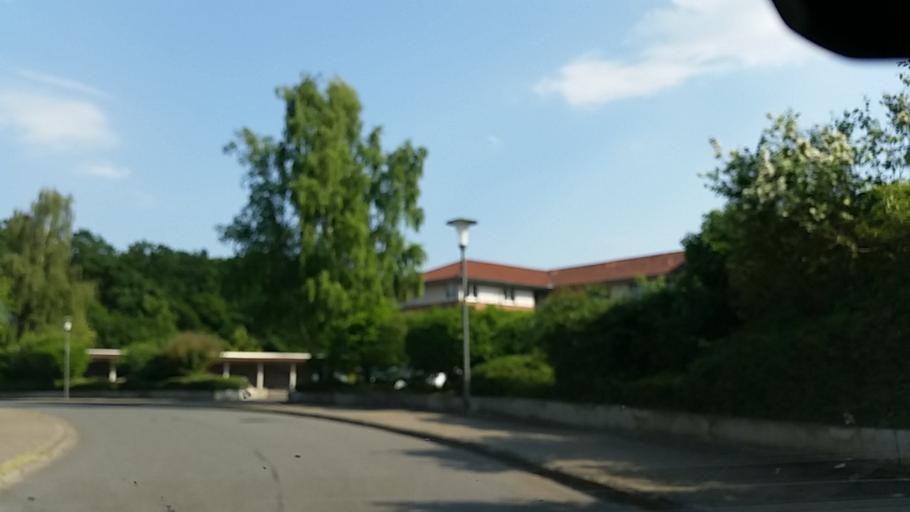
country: DE
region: Lower Saxony
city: Wolfsburg
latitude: 52.4084
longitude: 10.7492
